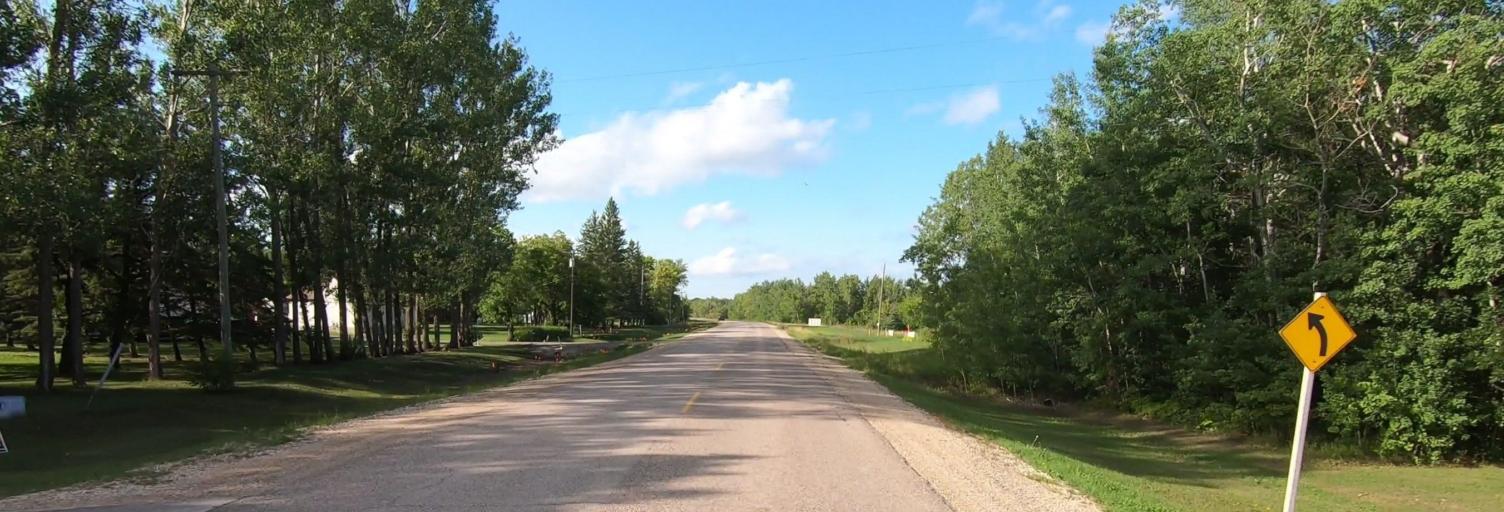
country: CA
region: Manitoba
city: Selkirk
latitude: 50.2204
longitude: -96.8388
